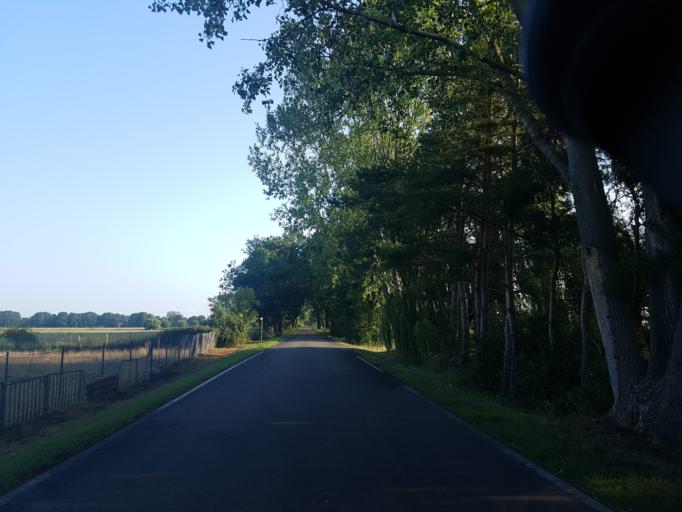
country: DE
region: Saxony-Anhalt
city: Holzdorf
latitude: 51.8144
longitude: 13.1461
